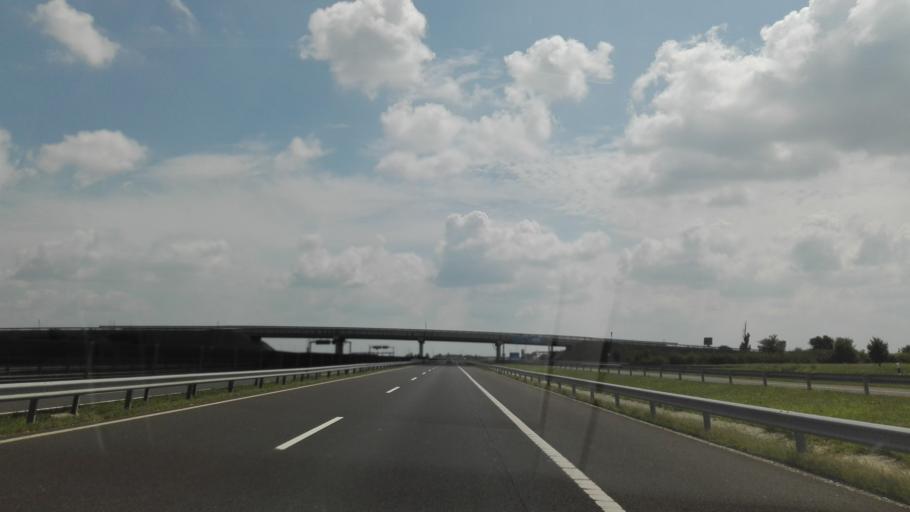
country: HU
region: Fejer
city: dunaujvaros
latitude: 46.9691
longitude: 18.8892
